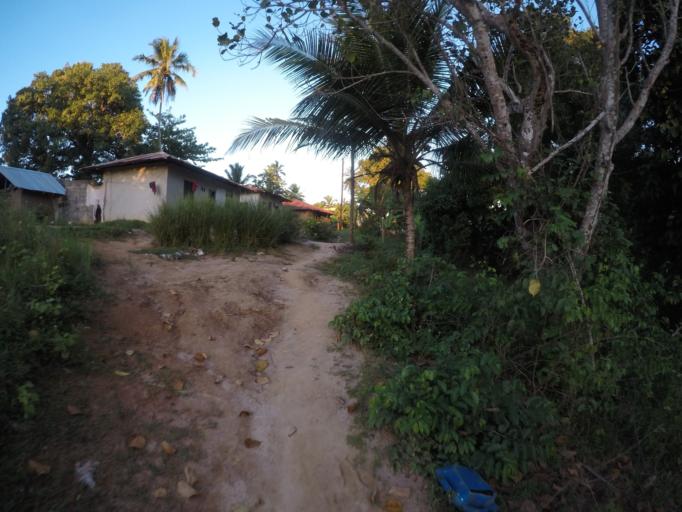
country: TZ
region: Pemba South
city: Mtambile
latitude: -5.3810
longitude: 39.7173
